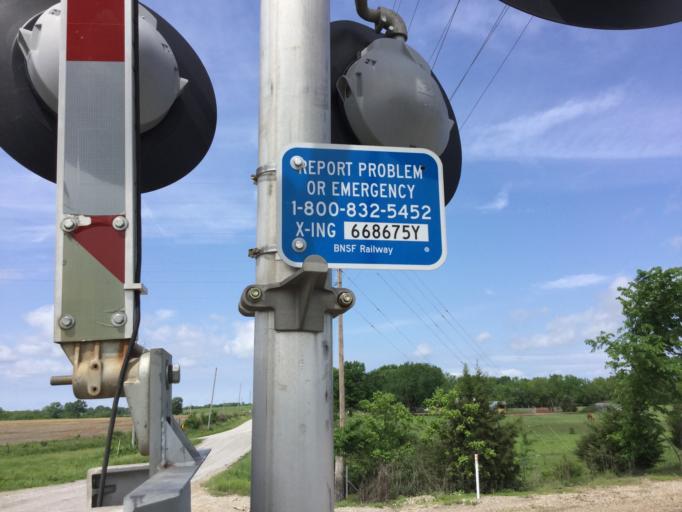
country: US
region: Kansas
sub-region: Linn County
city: Pleasanton
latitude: 38.1463
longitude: -94.6963
